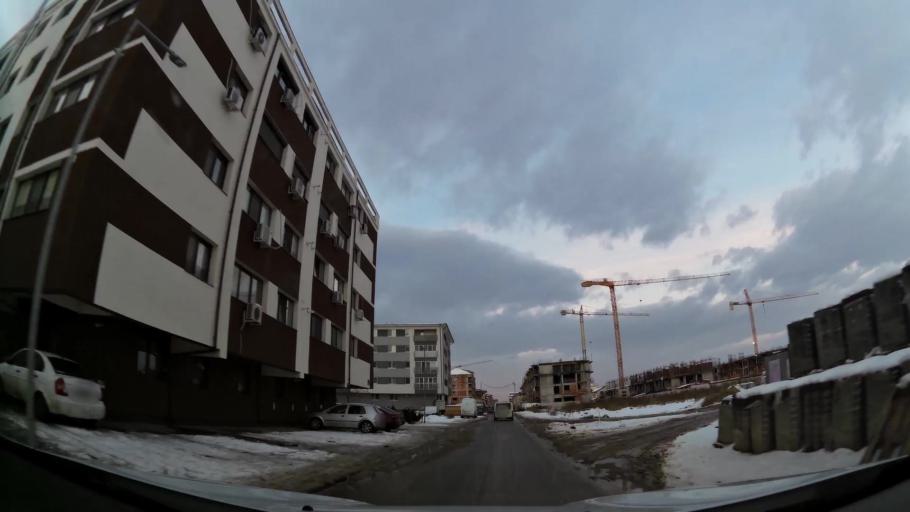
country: RO
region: Ilfov
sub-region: Comuna Popesti-Leordeni
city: Popesti-Leordeni
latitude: 44.3663
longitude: 26.1538
